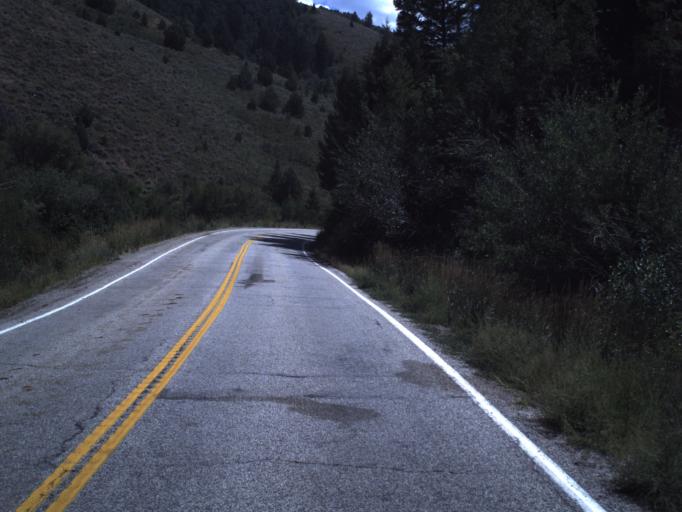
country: US
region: Utah
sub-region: Cache County
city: North Logan
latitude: 41.8520
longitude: -111.5857
